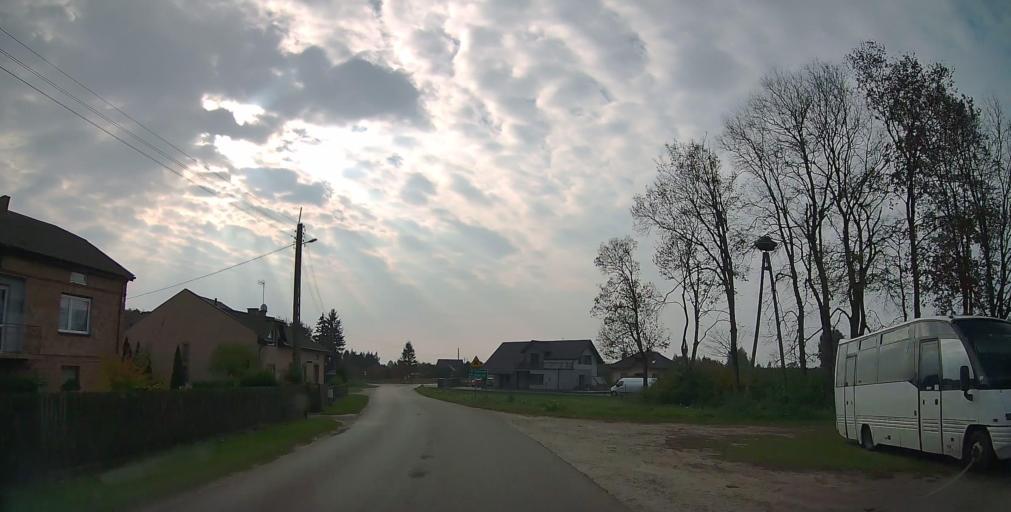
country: PL
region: Masovian Voivodeship
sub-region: Powiat grojecki
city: Mogielnica
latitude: 51.6617
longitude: 20.7109
